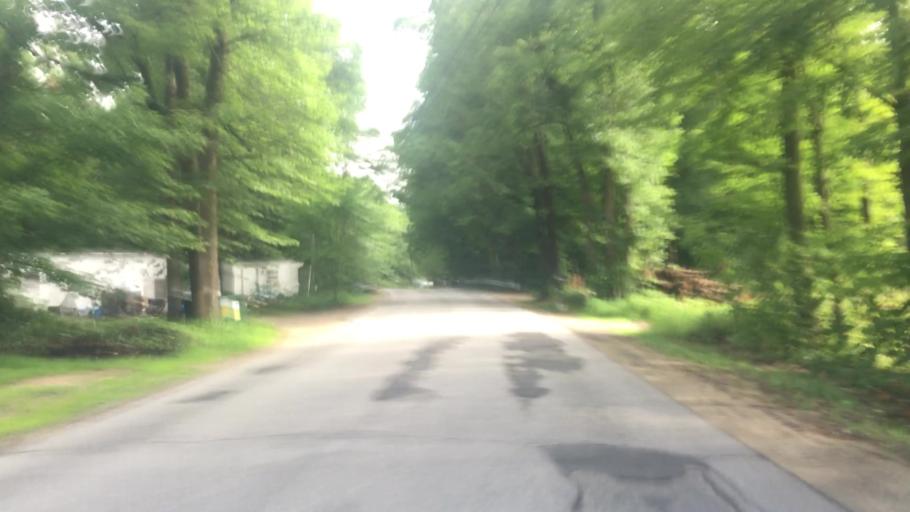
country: US
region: Maine
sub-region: Oxford County
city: South Paris
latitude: 44.2022
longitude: -70.5136
